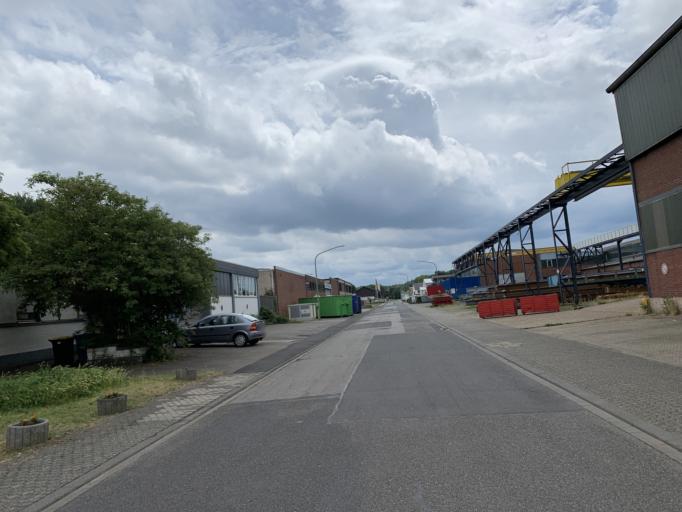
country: DE
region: North Rhine-Westphalia
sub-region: Regierungsbezirk Koln
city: Dueren
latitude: 50.7762
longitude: 6.4801
